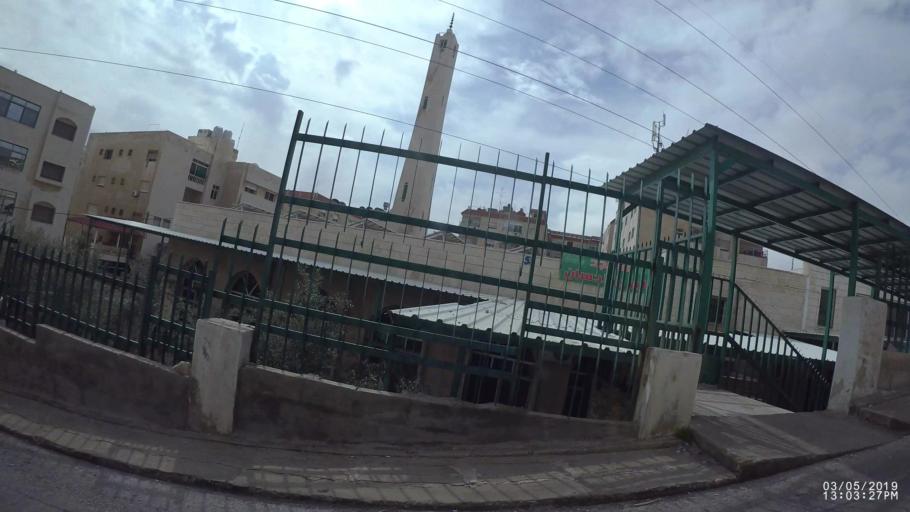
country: JO
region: Amman
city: Amman
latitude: 31.9981
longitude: 35.9336
